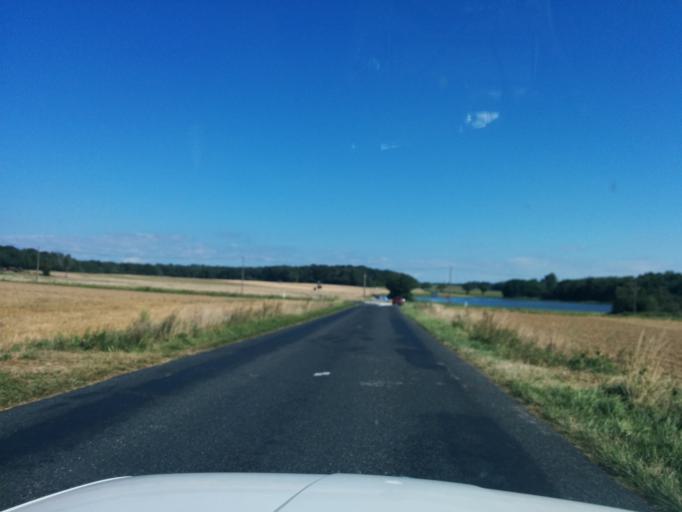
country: FR
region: Rhone-Alpes
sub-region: Departement de l'Ain
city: Chalamont
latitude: 45.9607
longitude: 5.1474
